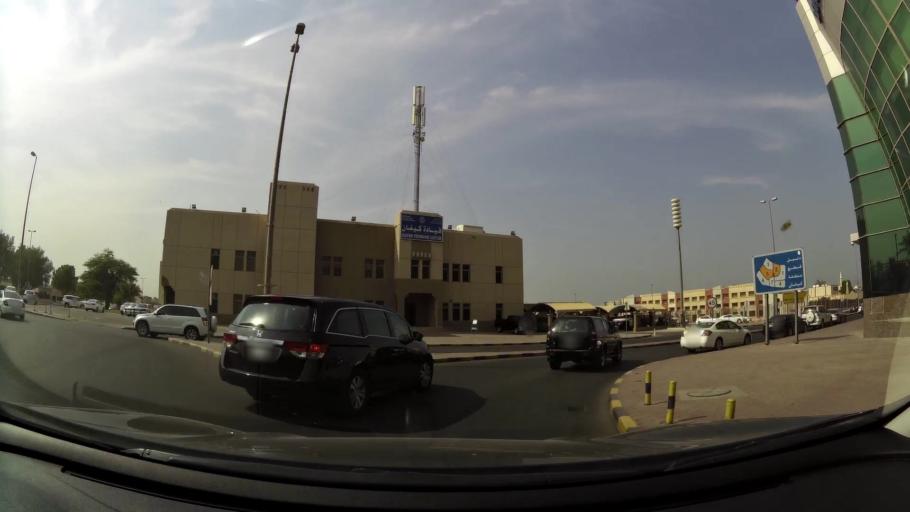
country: KW
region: Al Asimah
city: Ash Shamiyah
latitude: 29.3389
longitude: 47.9619
